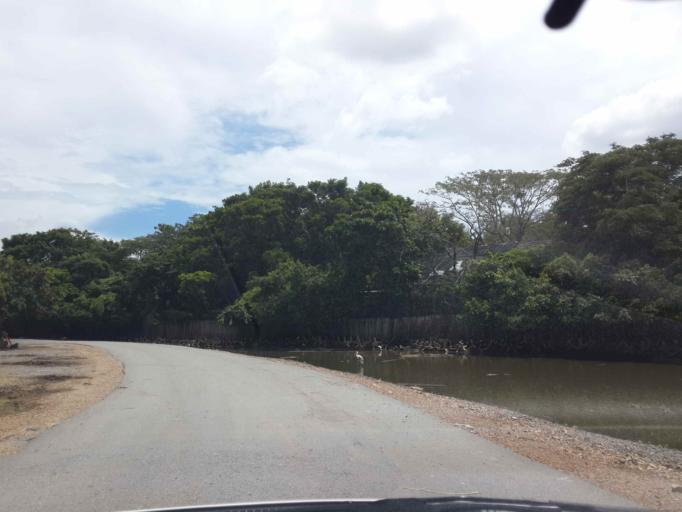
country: TH
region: Bangkok
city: Khan Na Yao
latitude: 13.8652
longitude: 100.7008
